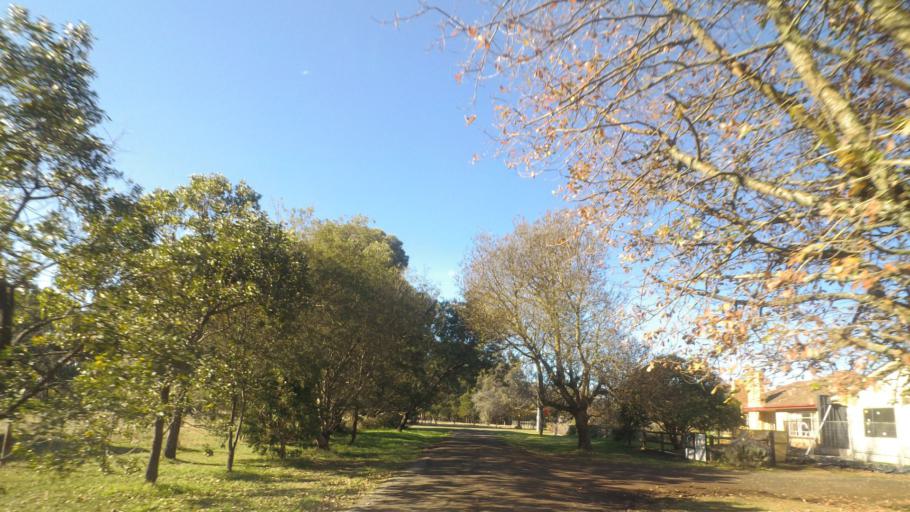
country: AU
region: Victoria
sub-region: Mount Alexander
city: Castlemaine
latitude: -37.3035
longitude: 144.3345
